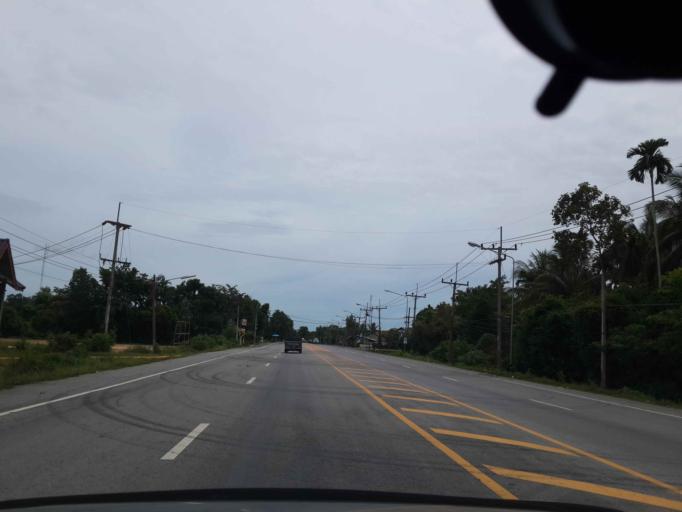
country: TH
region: Narathiwat
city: Yi-ngo
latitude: 6.3963
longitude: 101.6953
